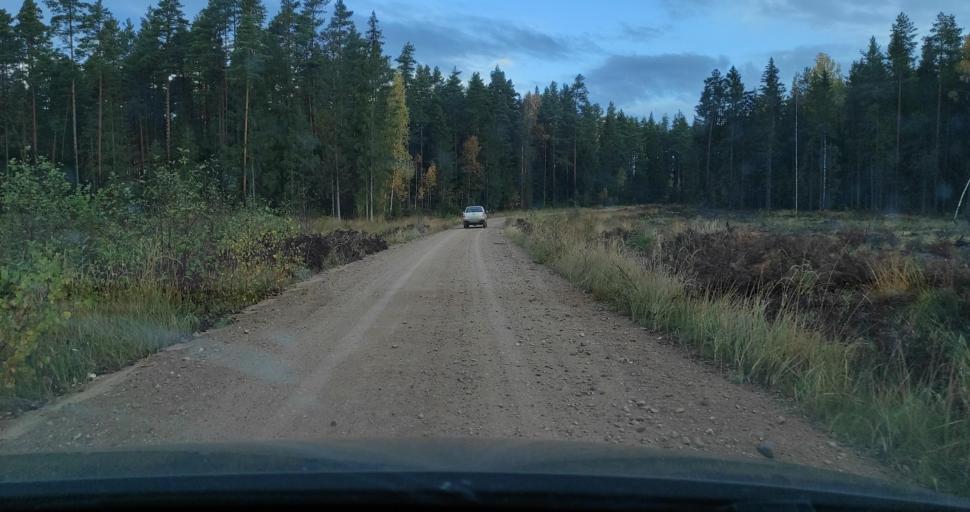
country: LV
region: Kuldigas Rajons
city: Kuldiga
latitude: 57.0369
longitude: 22.0644
